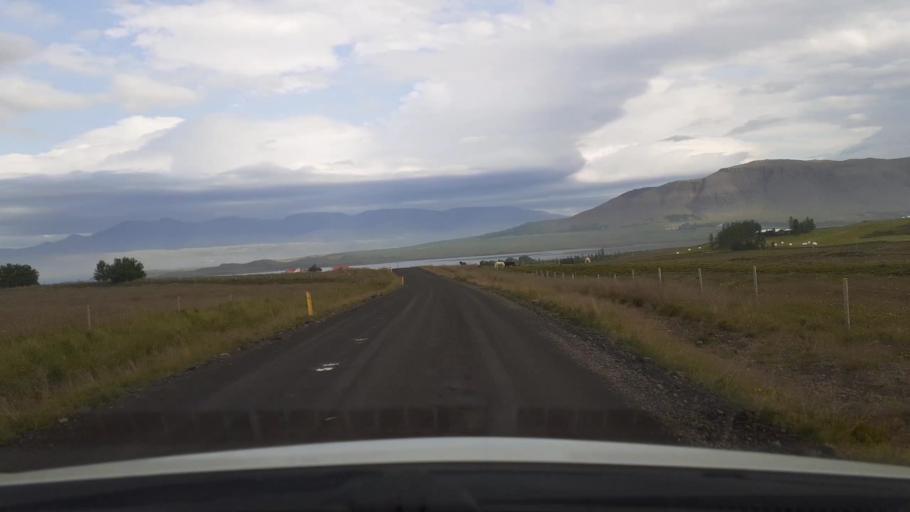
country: IS
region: Capital Region
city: Mosfellsbaer
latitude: 64.3221
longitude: -21.6496
